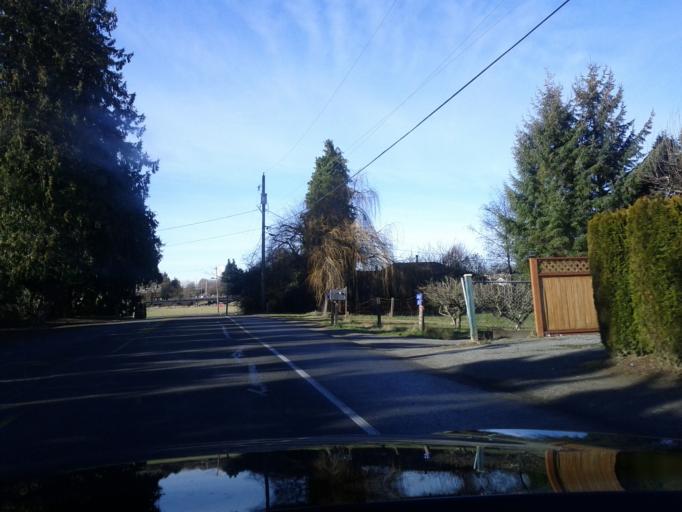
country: US
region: Washington
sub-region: Skagit County
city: Burlington
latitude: 48.4644
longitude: -122.3228
